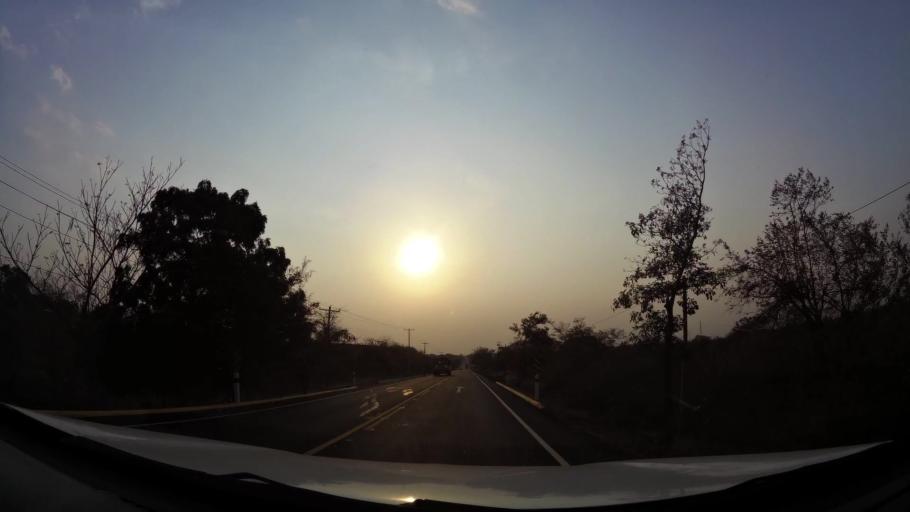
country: NI
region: Leon
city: Nagarote
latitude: 12.2684
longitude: -86.5508
